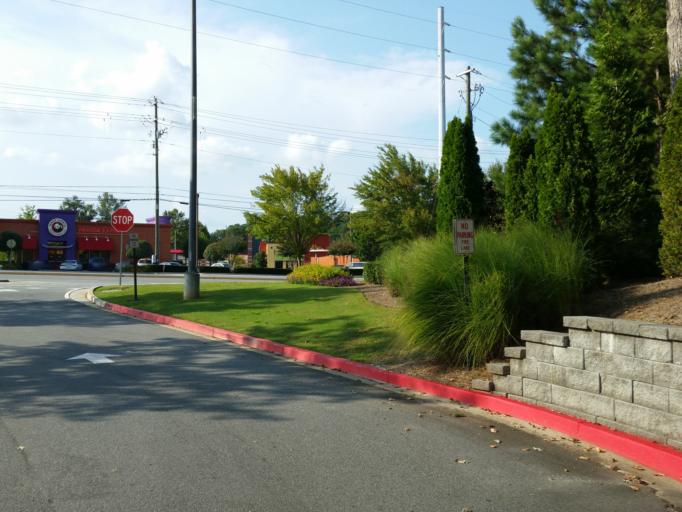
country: US
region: Georgia
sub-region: Fulton County
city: Roswell
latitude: 33.9841
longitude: -84.4258
